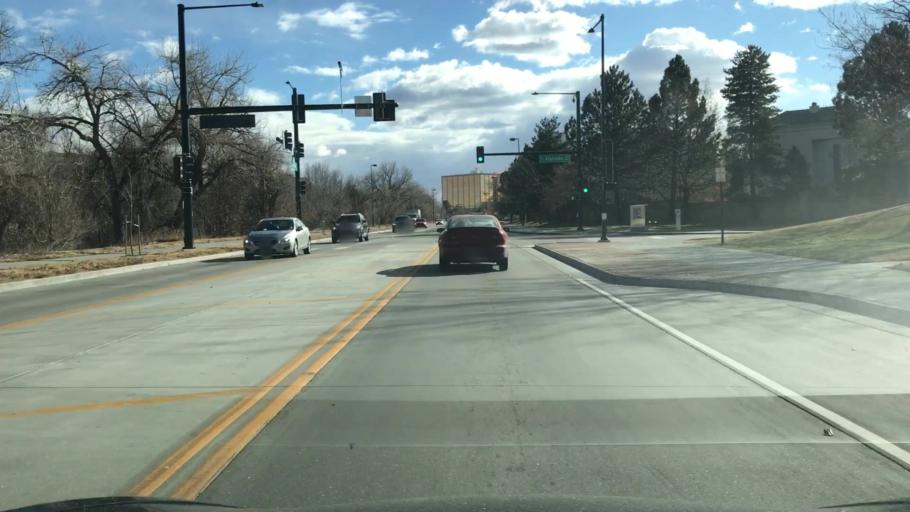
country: US
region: Colorado
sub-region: Arapahoe County
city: Glendale
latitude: 39.7116
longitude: -104.9488
